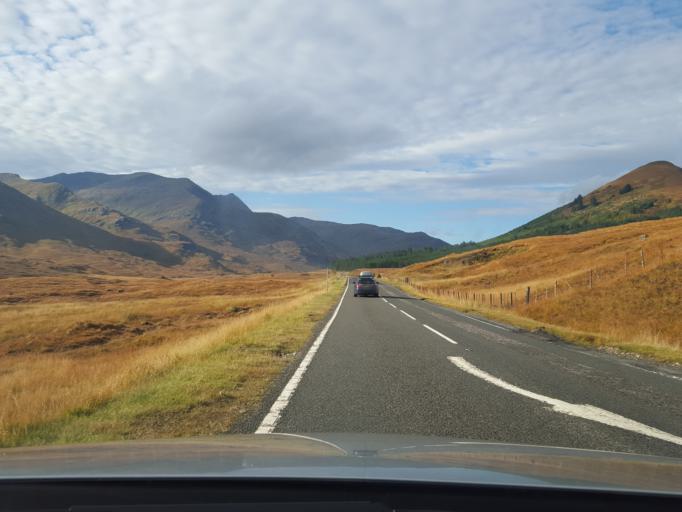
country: GB
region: Scotland
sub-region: Highland
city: Fort William
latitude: 57.1530
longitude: -5.2017
